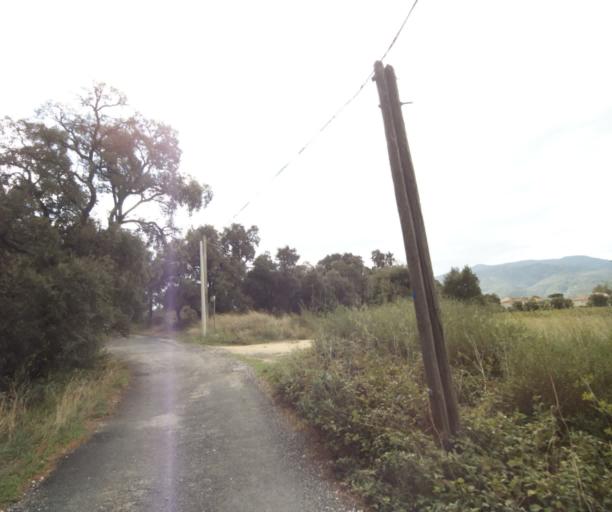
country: FR
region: Languedoc-Roussillon
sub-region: Departement des Pyrenees-Orientales
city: Argelers
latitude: 42.5565
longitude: 3.0174
